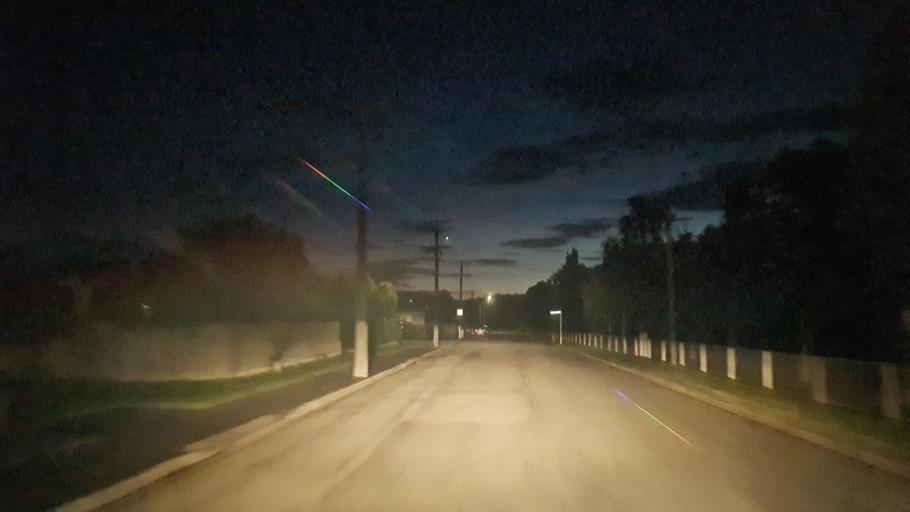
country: NZ
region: Otago
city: Oamaru
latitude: -45.0679
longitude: 170.9873
